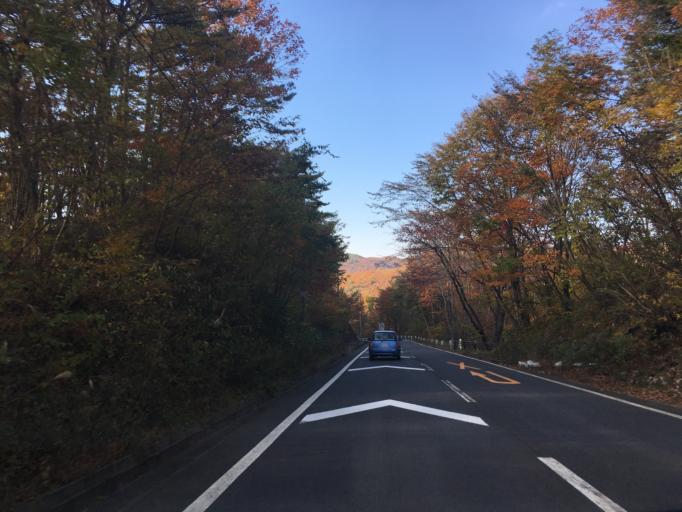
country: JP
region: Fukushima
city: Sukagawa
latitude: 37.2641
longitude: 140.0996
